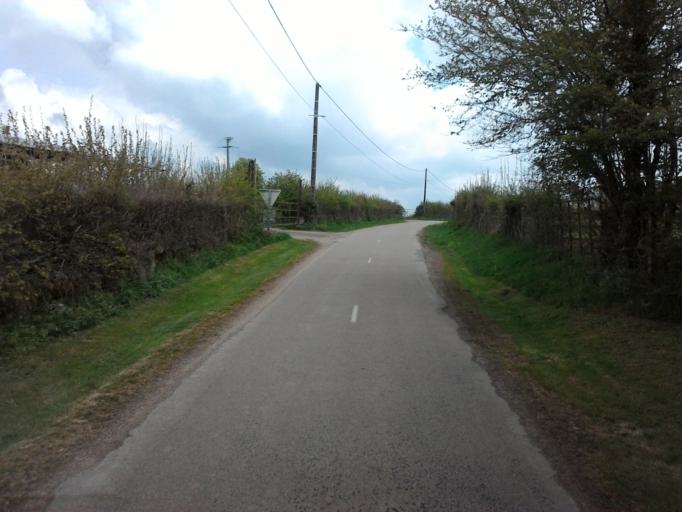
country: FR
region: Bourgogne
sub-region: Departement de la Cote-d'Or
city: Saulieu
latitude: 47.2354
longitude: 4.2159
